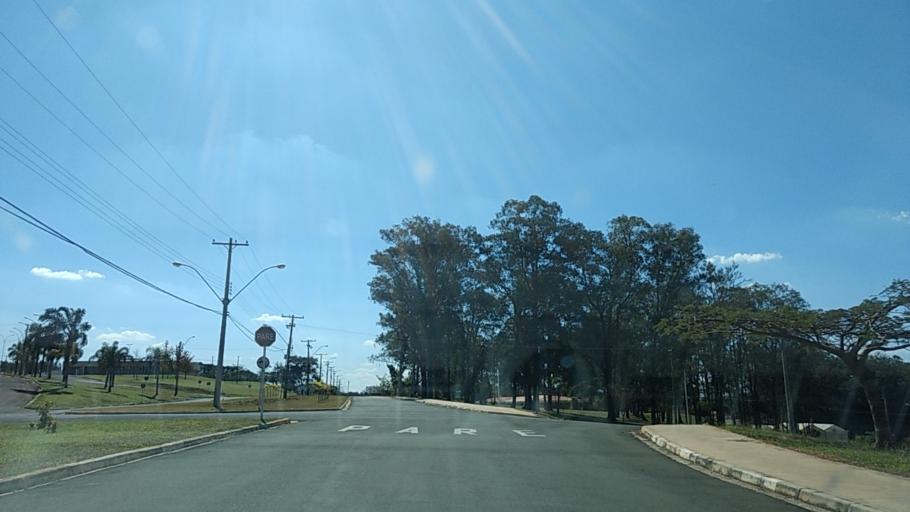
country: BR
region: Sao Paulo
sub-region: Botucatu
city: Botucatu
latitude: -22.8523
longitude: -48.4329
